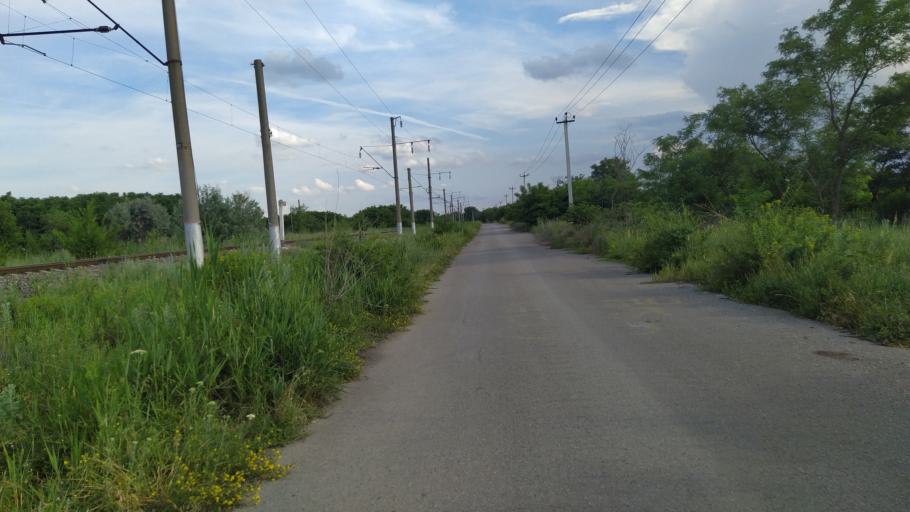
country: RU
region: Rostov
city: Bataysk
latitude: 47.1129
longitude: 39.7108
